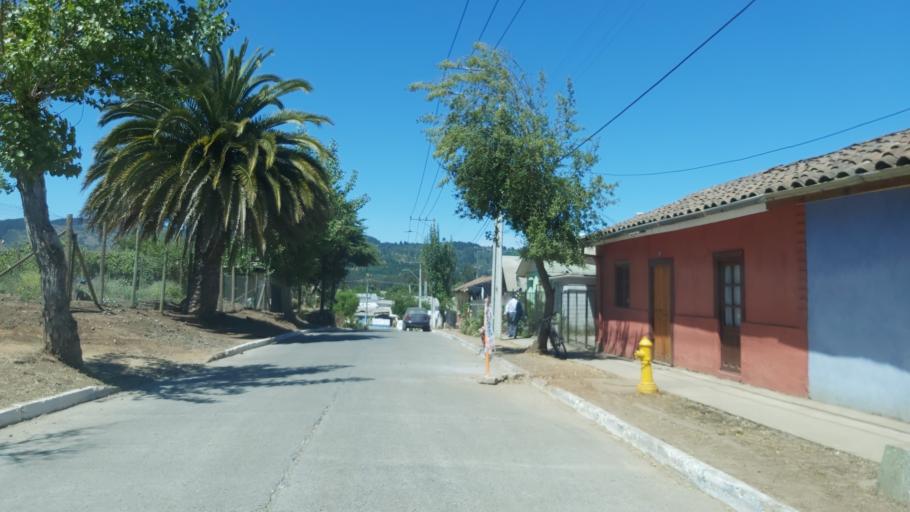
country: CL
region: Maule
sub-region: Provincia de Talca
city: Talca
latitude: -34.9838
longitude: -71.9824
